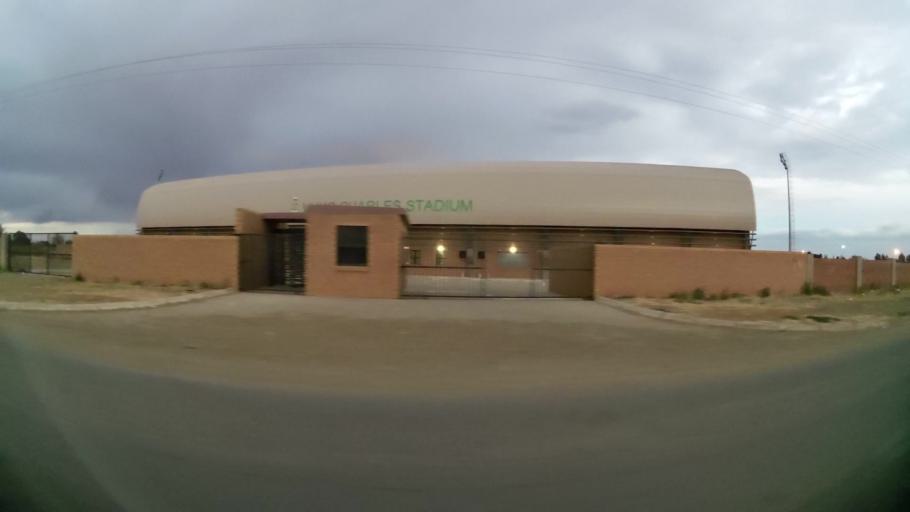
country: ZA
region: Orange Free State
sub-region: Lejweleputswa District Municipality
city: Welkom
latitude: -27.9583
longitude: 26.7856
